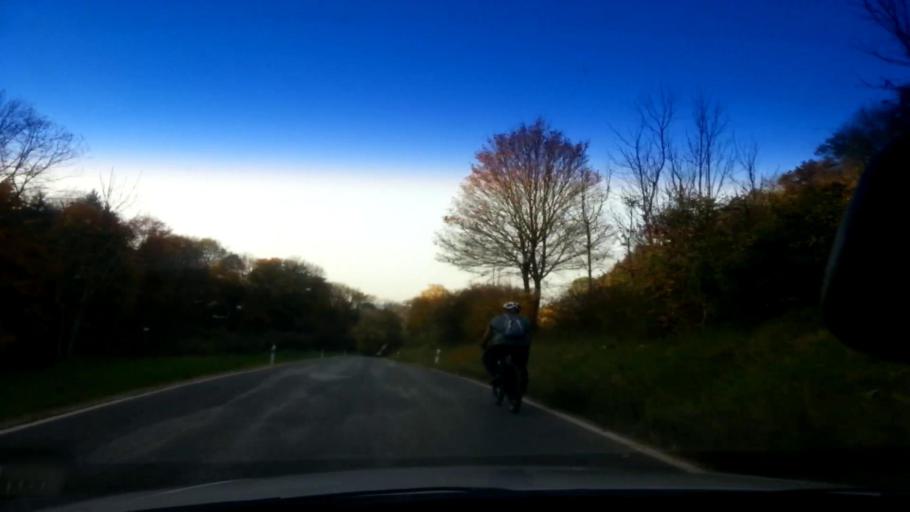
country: DE
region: Bavaria
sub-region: Upper Franconia
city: Schesslitz
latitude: 49.9549
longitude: 11.0643
